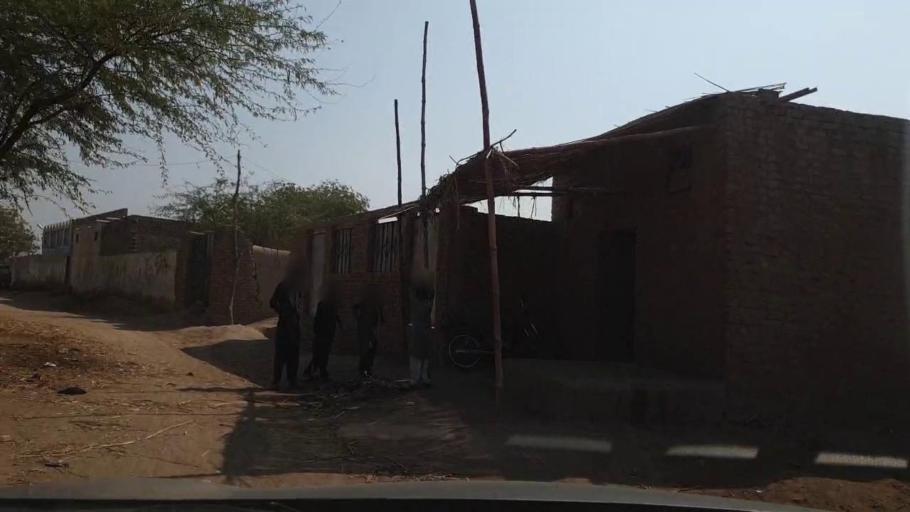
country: PK
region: Sindh
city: Tando Allahyar
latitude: 25.5381
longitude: 68.8133
